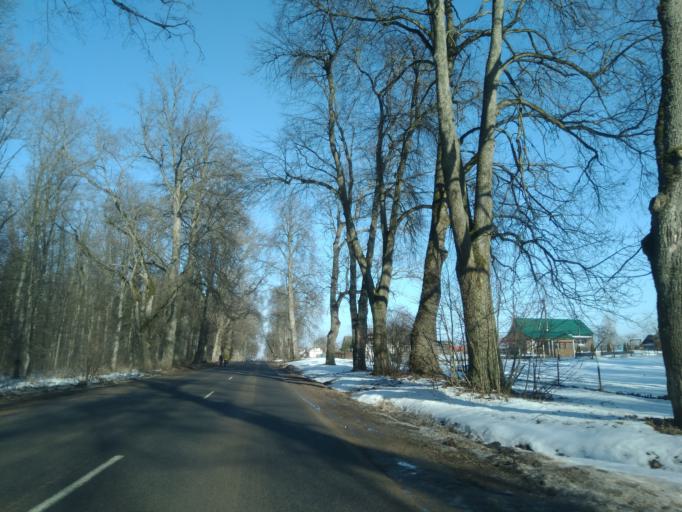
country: BY
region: Minsk
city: Nyasvizh
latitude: 53.2036
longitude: 26.6581
